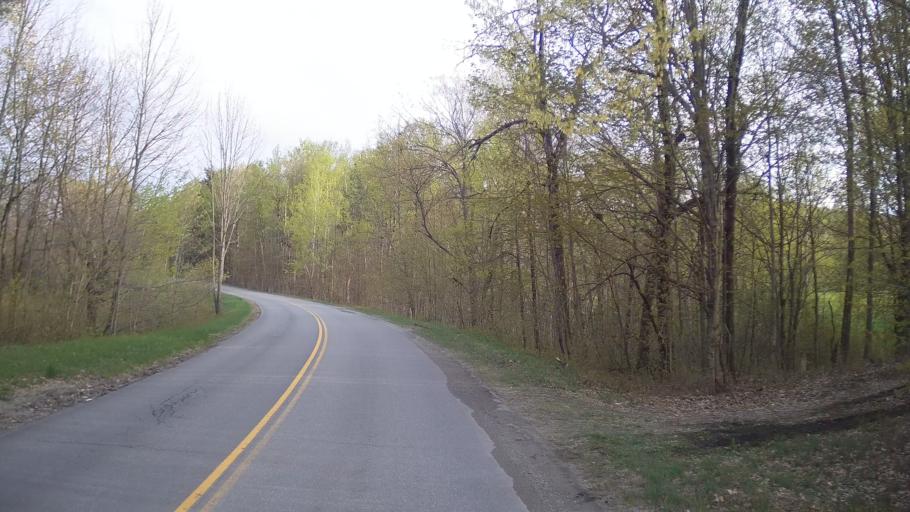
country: US
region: Vermont
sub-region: Orleans County
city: Newport
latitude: 44.9422
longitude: -72.4381
